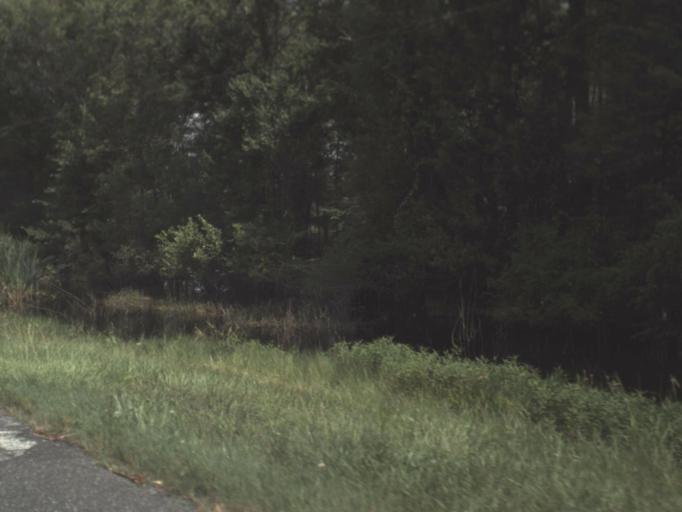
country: US
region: Florida
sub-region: Taylor County
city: Perry
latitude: 29.9698
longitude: -83.4786
